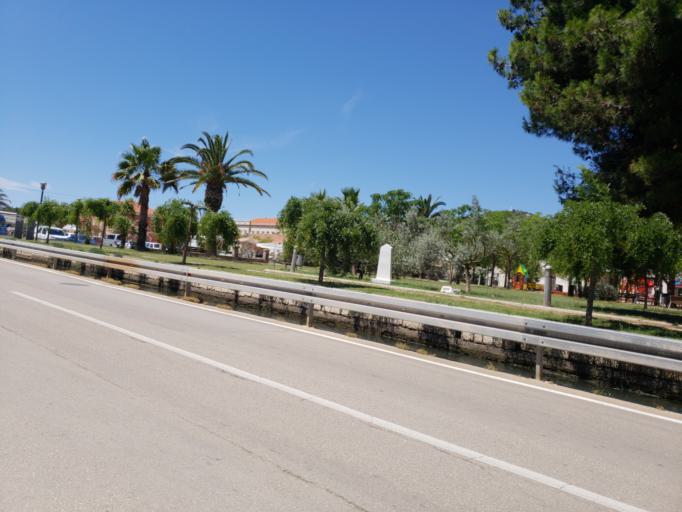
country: HR
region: Splitsko-Dalmatinska
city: Stari Grad
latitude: 43.1842
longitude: 16.6004
